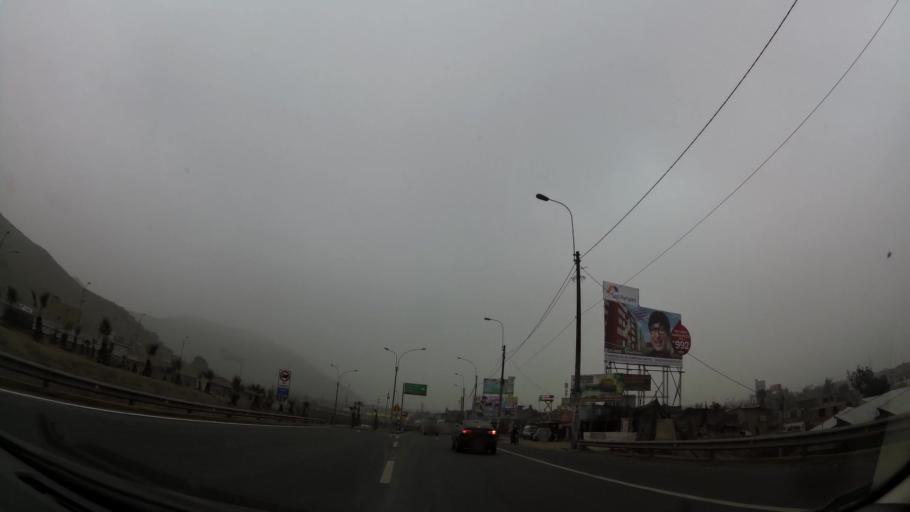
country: PE
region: Lima
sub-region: Lima
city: Santa Maria
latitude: -12.0141
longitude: -76.9027
